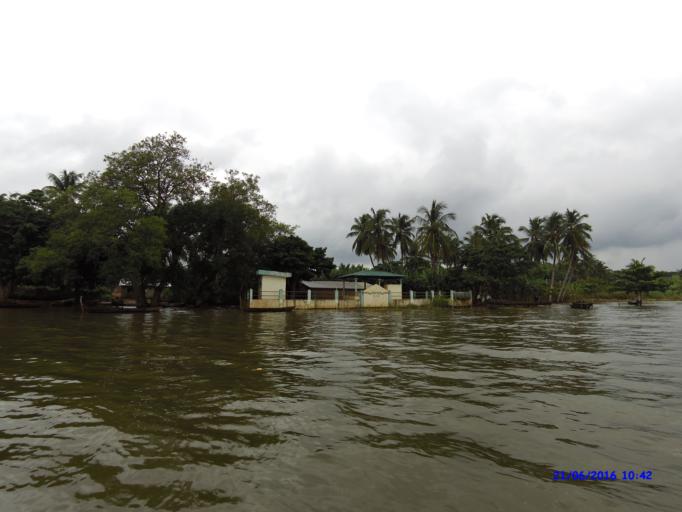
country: BJ
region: Mono
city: Come
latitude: 6.4875
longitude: 1.9521
